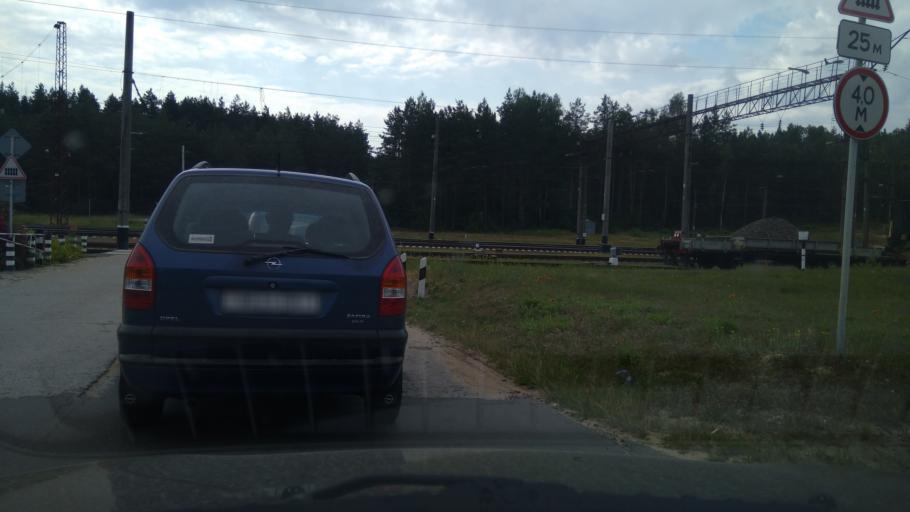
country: BY
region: Brest
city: Nyakhachava
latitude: 52.6048
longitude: 25.0855
